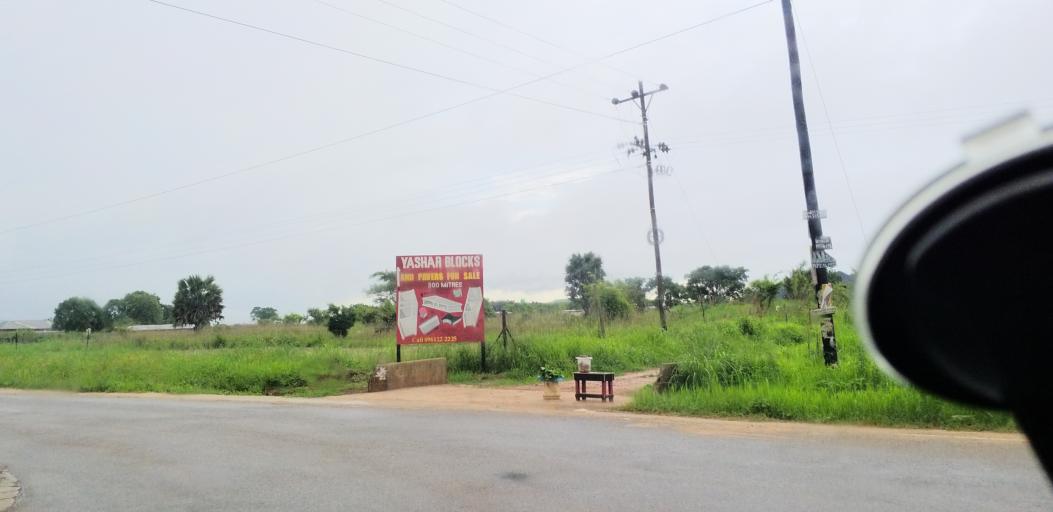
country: ZM
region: Lusaka
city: Lusaka
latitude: -15.5138
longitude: 28.3112
